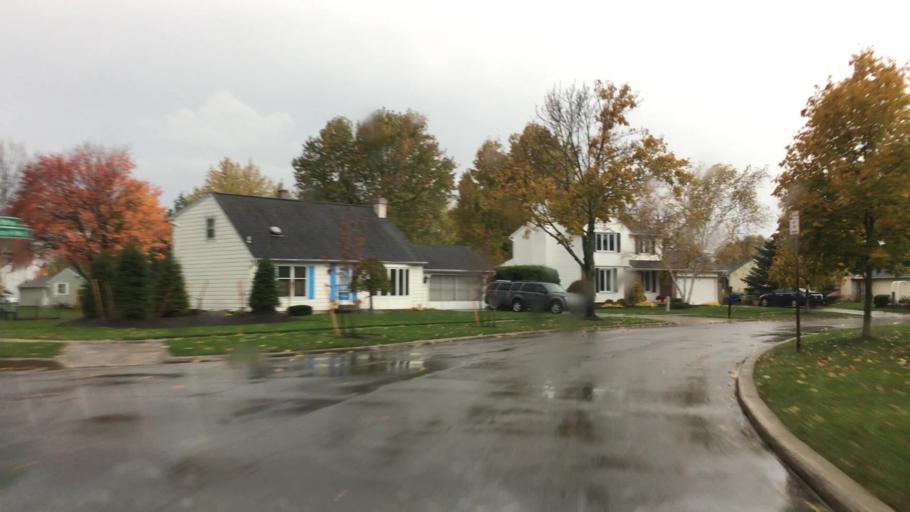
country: US
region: New York
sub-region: Erie County
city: Lancaster
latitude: 42.8744
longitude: -78.6780
